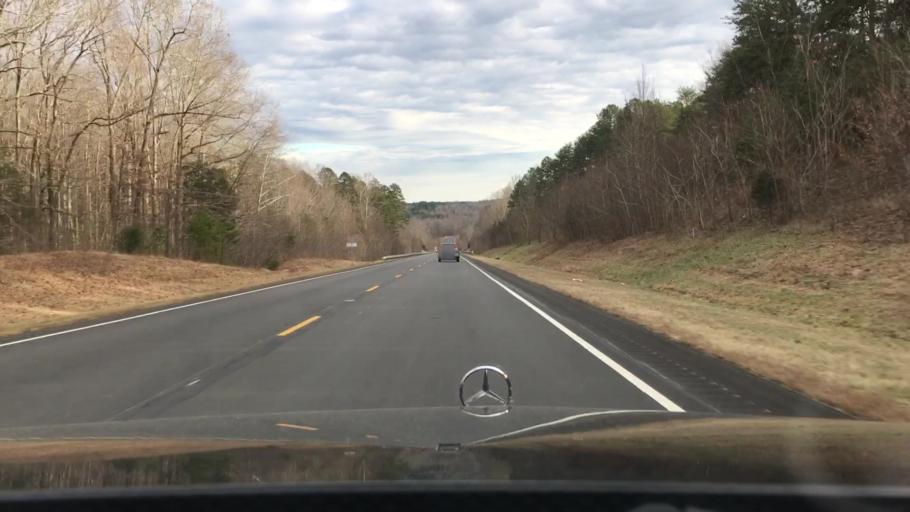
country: US
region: North Carolina
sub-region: Caswell County
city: Yanceyville
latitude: 36.3237
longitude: -79.2339
